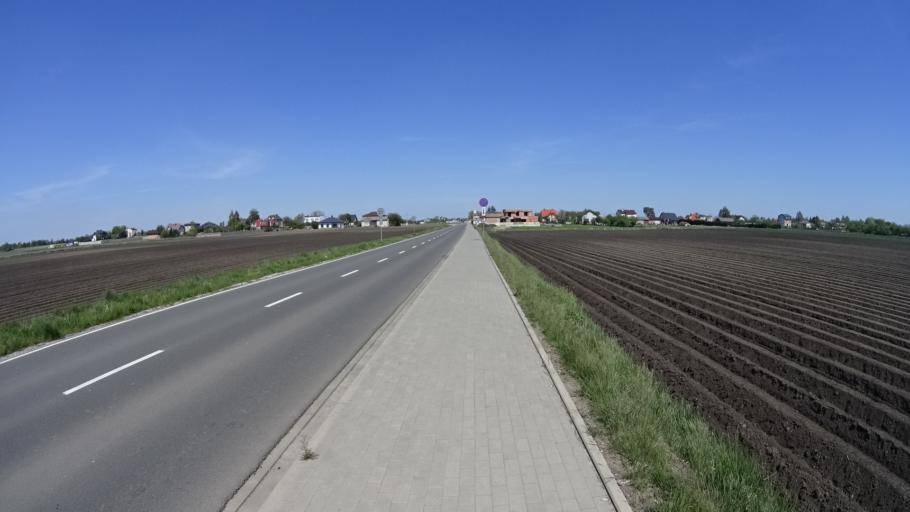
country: PL
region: Masovian Voivodeship
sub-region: Powiat warszawski zachodni
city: Jozefow
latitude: 52.2379
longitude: 20.7378
